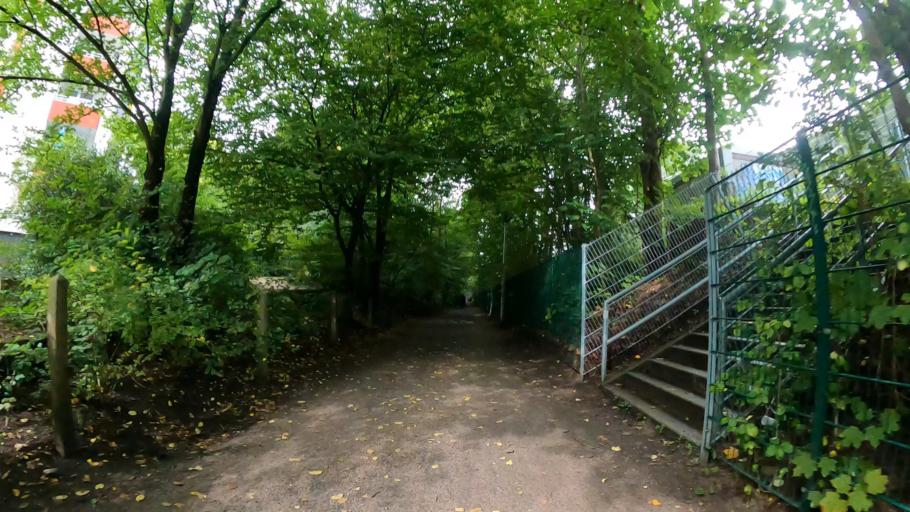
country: DE
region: Schleswig-Holstein
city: Rellingen
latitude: 53.6527
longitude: 9.8010
